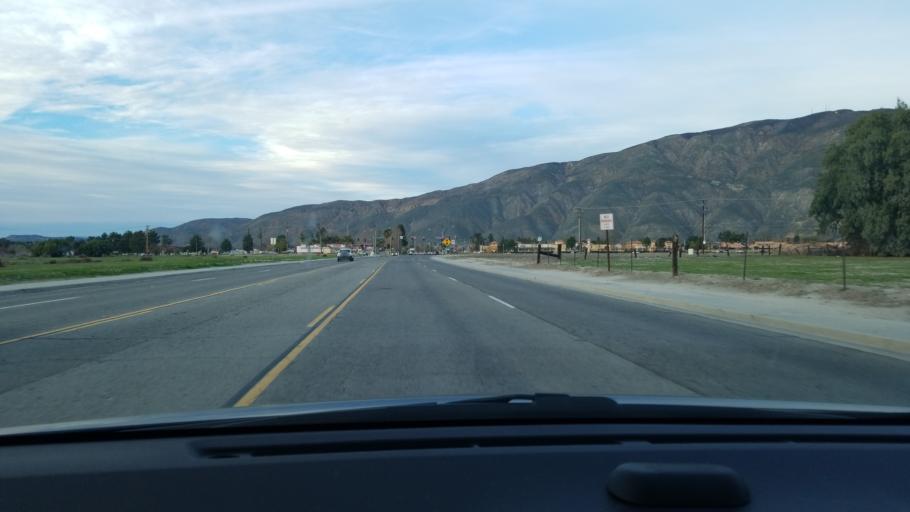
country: US
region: California
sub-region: Riverside County
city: San Jacinto
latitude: 33.7974
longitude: -116.9717
